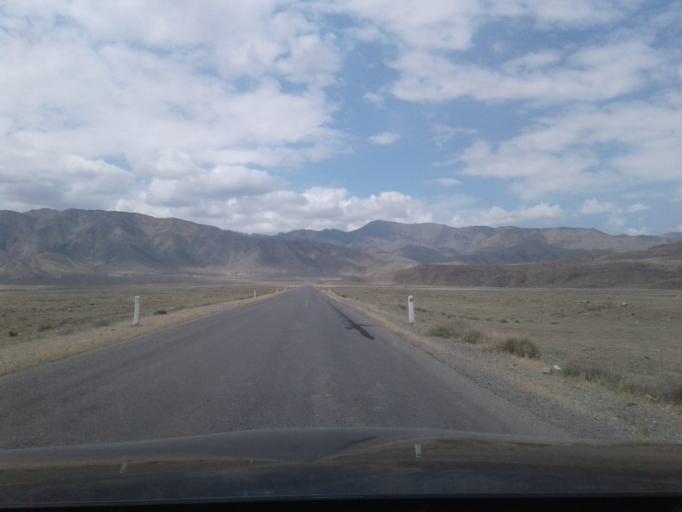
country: TM
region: Ahal
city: Baharly
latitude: 38.5199
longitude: 57.1387
